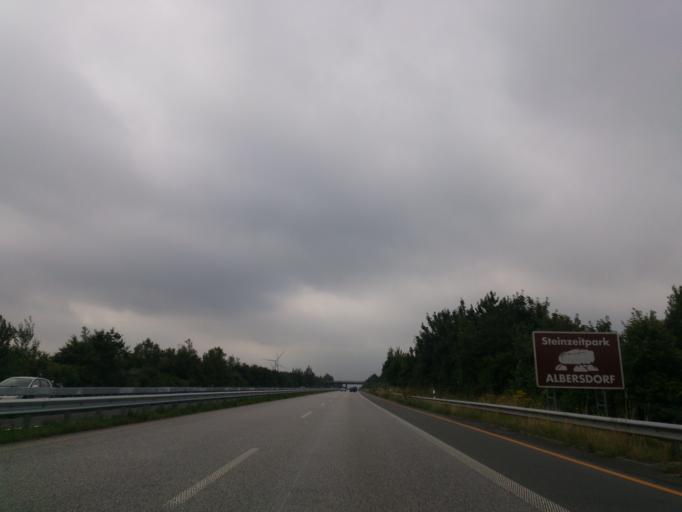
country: DE
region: Schleswig-Holstein
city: Arkebek
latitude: 54.1333
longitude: 9.2526
